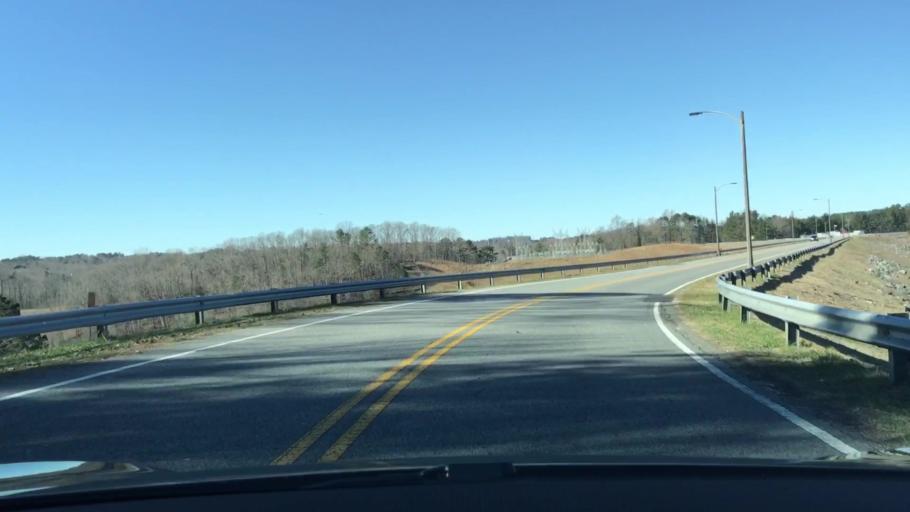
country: US
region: Georgia
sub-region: Gwinnett County
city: Sugar Hill
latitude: 34.1585
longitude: -84.0725
